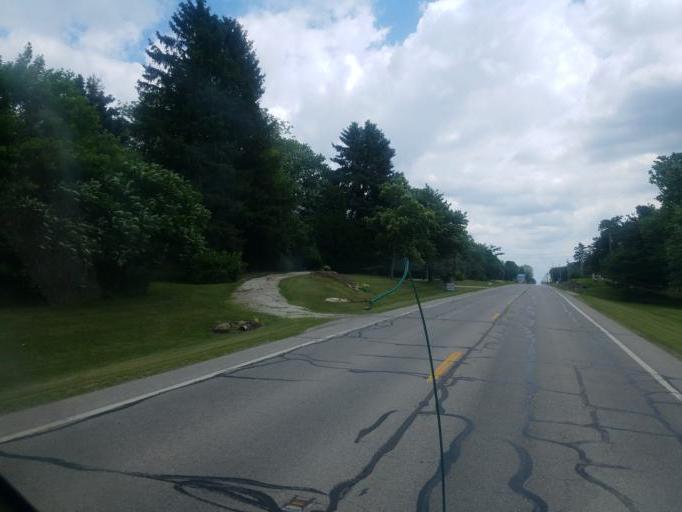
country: US
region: Ohio
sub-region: Huron County
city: Plymouth
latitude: 41.0312
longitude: -82.6136
